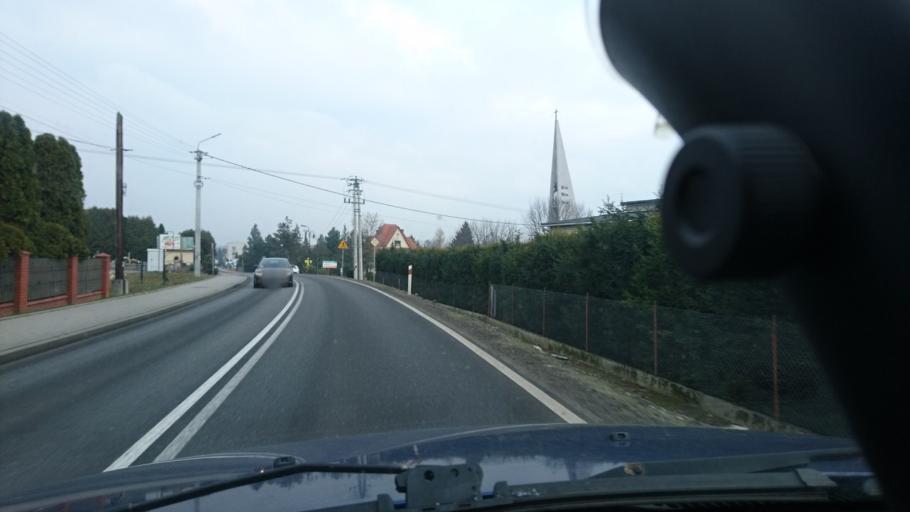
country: PL
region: Silesian Voivodeship
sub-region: Powiat bielski
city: Pisarzowice
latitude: 49.8787
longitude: 19.1368
